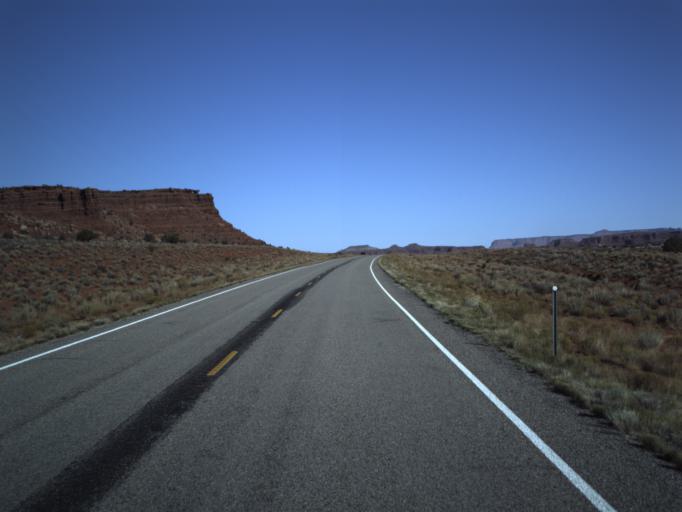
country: US
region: Utah
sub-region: San Juan County
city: Blanding
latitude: 37.7658
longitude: -110.2856
